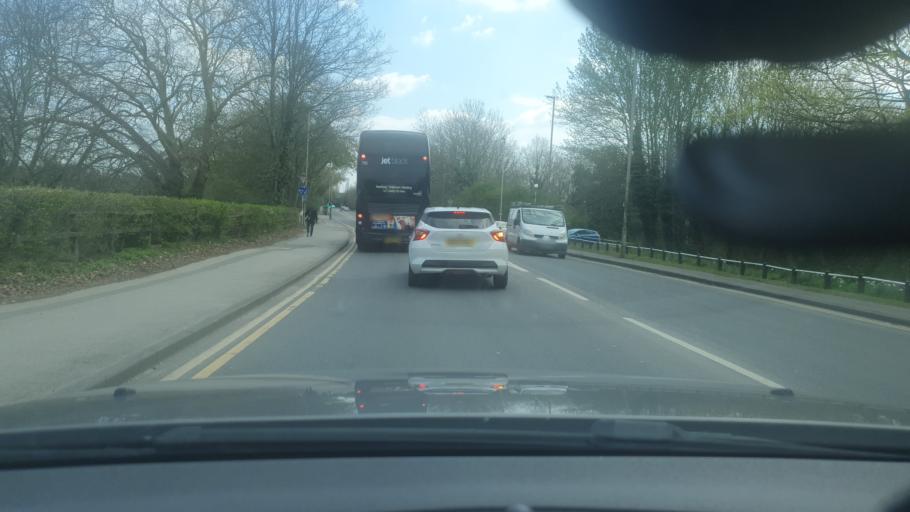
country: GB
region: England
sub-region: West Berkshire
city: Tilehurst
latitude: 51.4457
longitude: -1.0102
